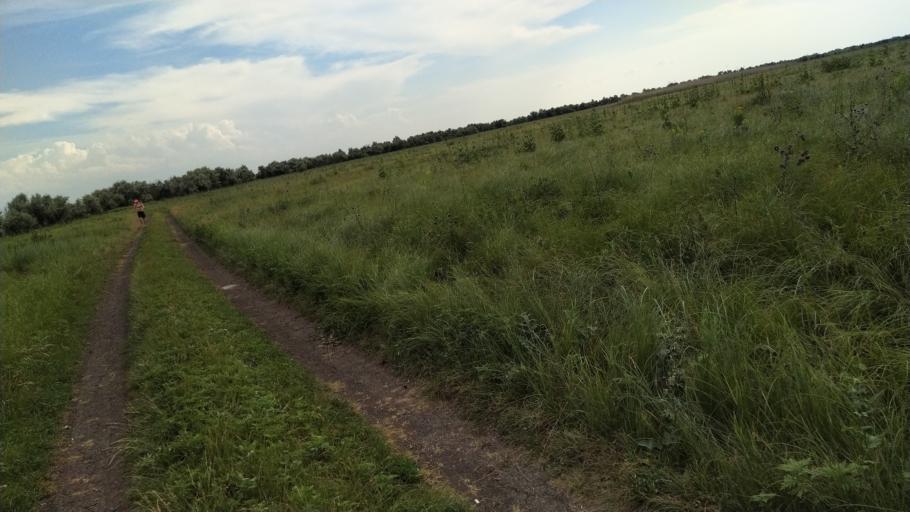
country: RU
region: Rostov
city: Kuleshovka
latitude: 47.1270
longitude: 39.6291
